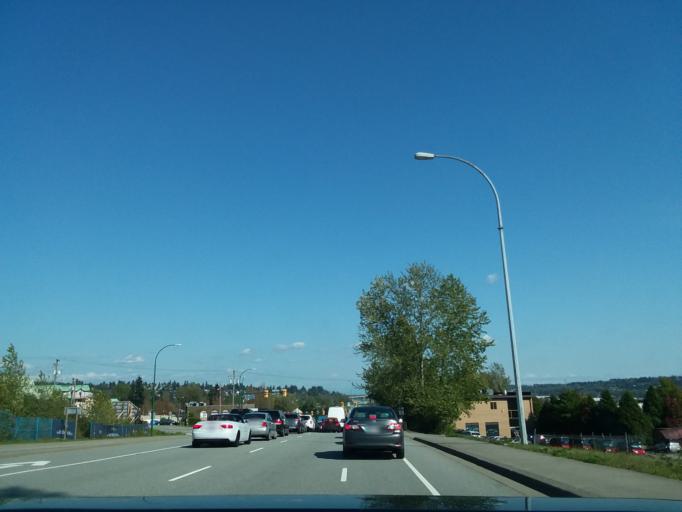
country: CA
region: British Columbia
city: New Westminster
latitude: 49.2372
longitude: -122.8749
